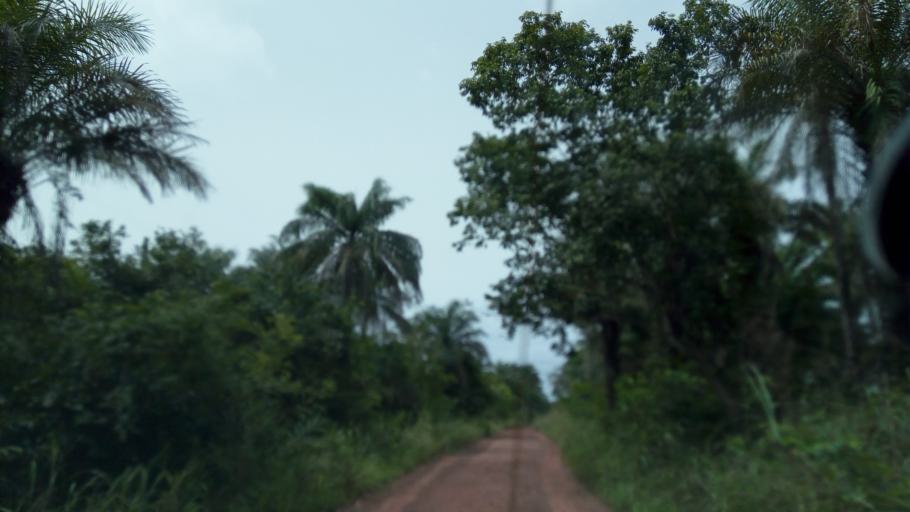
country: SL
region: Northern Province
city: Kambia
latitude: 9.0940
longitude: -13.0150
